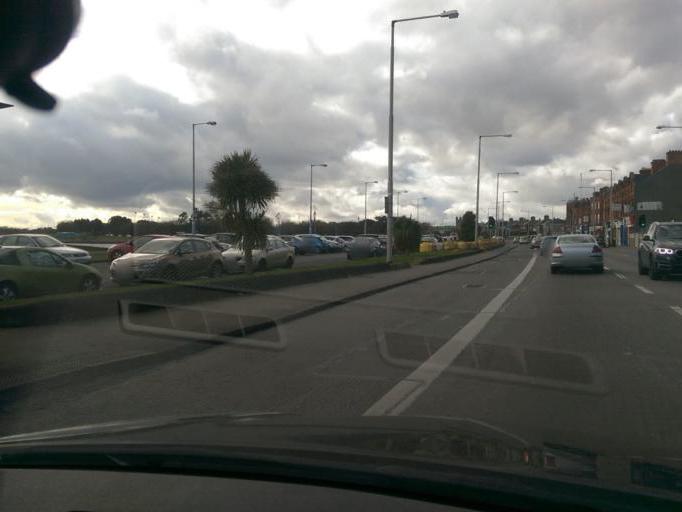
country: IE
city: Donnycarney
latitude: 53.3622
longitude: -6.2169
